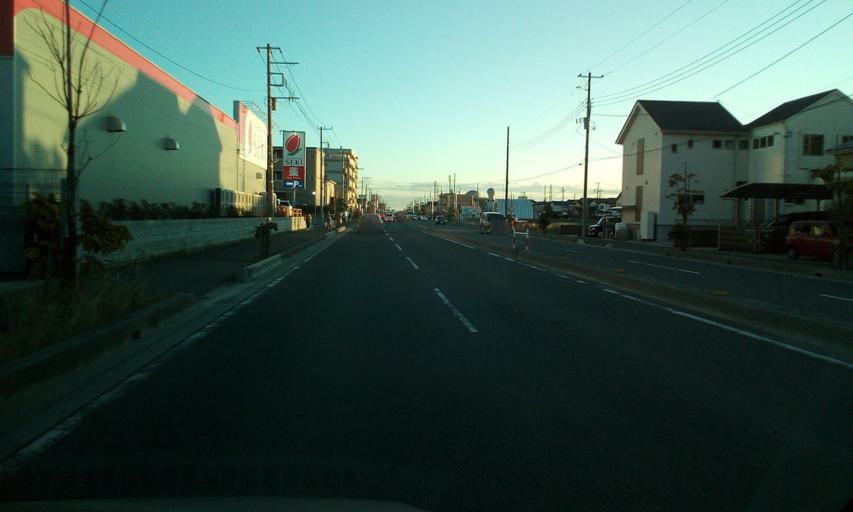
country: JP
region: Saitama
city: Yoshikawa
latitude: 35.8729
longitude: 139.8478
